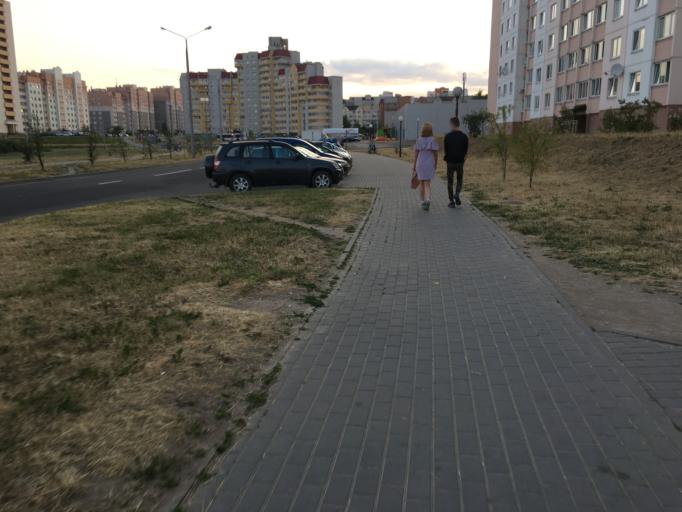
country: BY
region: Grodnenskaya
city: Hrodna
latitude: 53.7114
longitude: 23.8623
